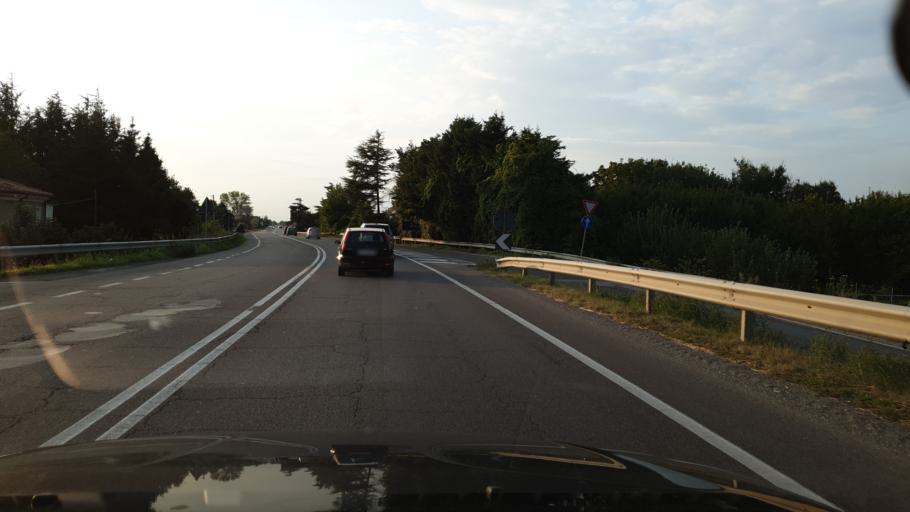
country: IT
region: Emilia-Romagna
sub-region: Provincia di Rimini
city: Santa Giustina
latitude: 44.0855
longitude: 12.5201
